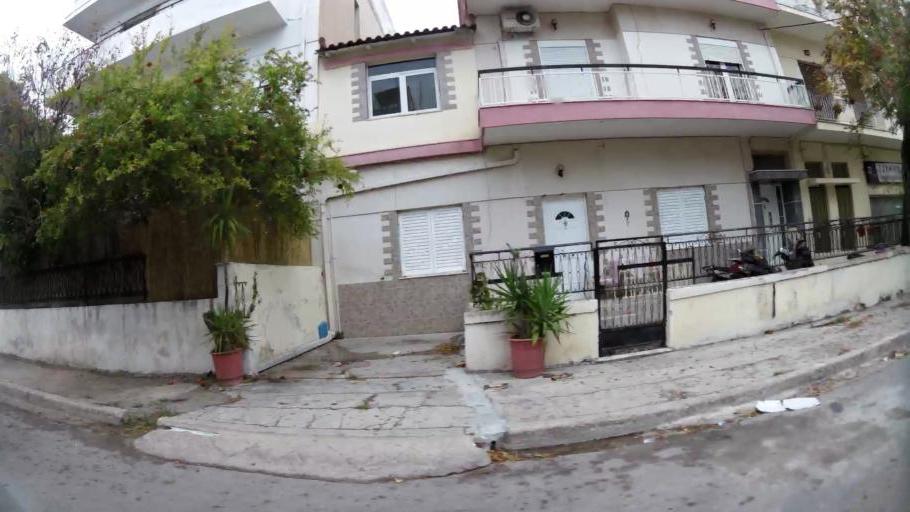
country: GR
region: Attica
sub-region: Nomarchia Athinas
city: Ilion
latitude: 38.0335
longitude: 23.7119
